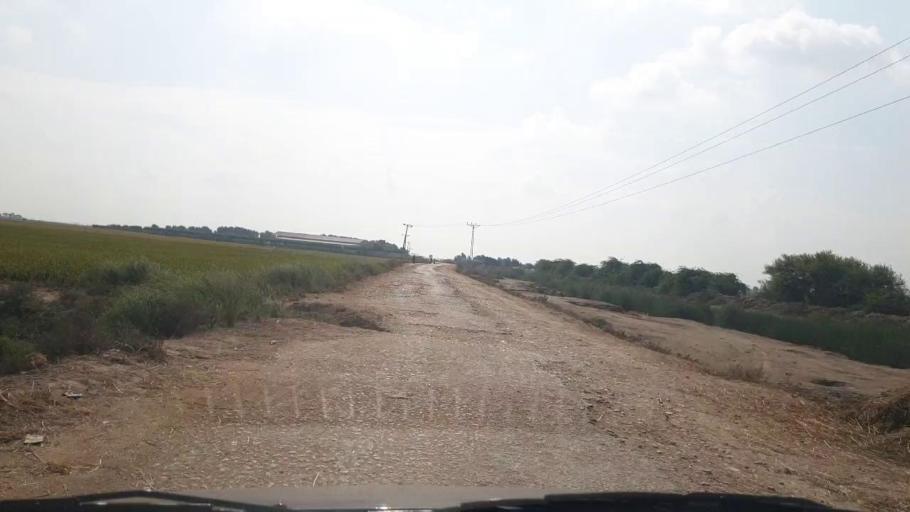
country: PK
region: Sindh
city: Kario
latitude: 24.6404
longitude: 68.5457
